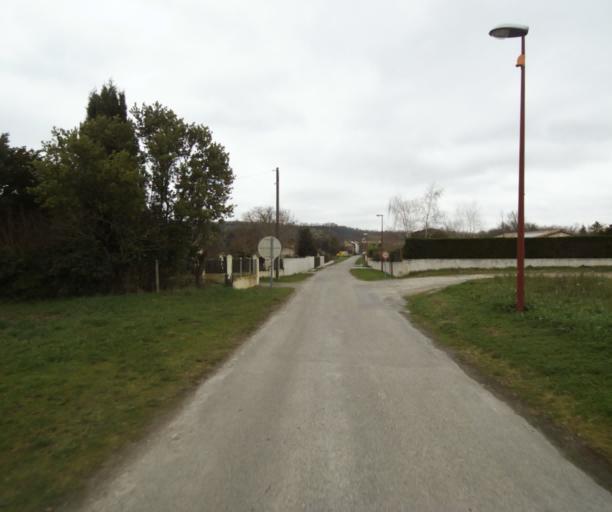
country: FR
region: Midi-Pyrenees
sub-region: Departement de l'Ariege
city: Saverdun
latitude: 43.1825
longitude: 1.6087
